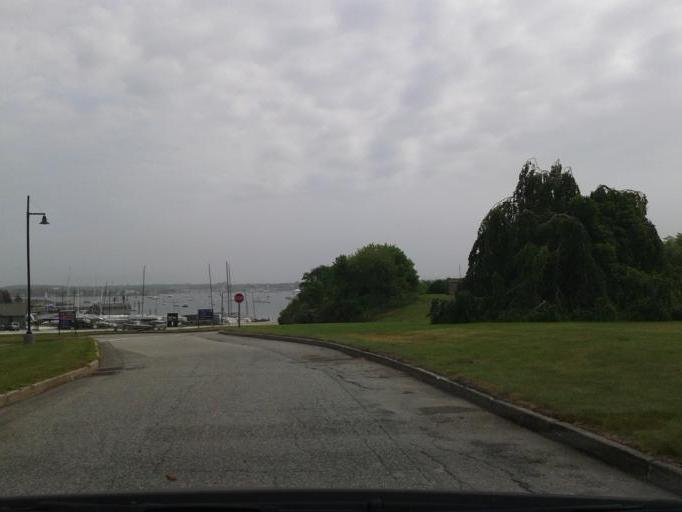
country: US
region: Rhode Island
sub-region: Newport County
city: Newport
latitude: 41.4705
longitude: -71.3394
